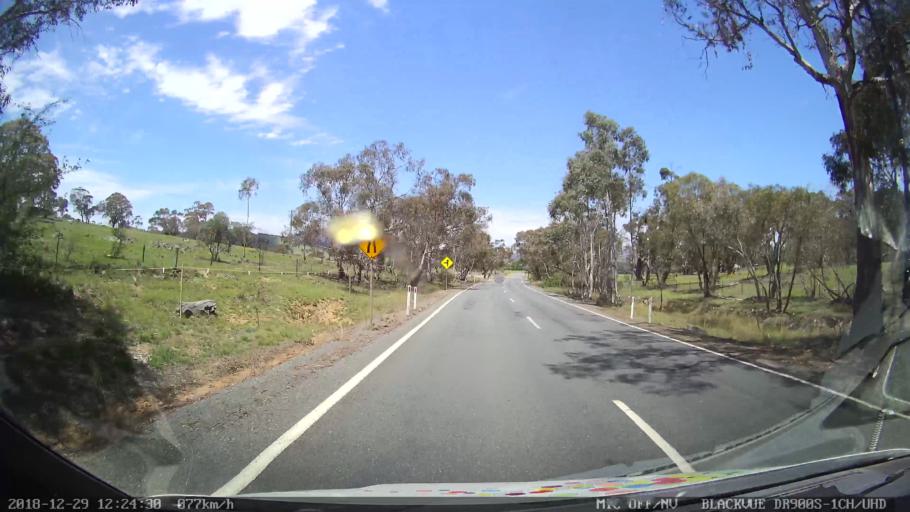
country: AU
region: Australian Capital Territory
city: Macarthur
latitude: -35.4476
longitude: 149.2107
